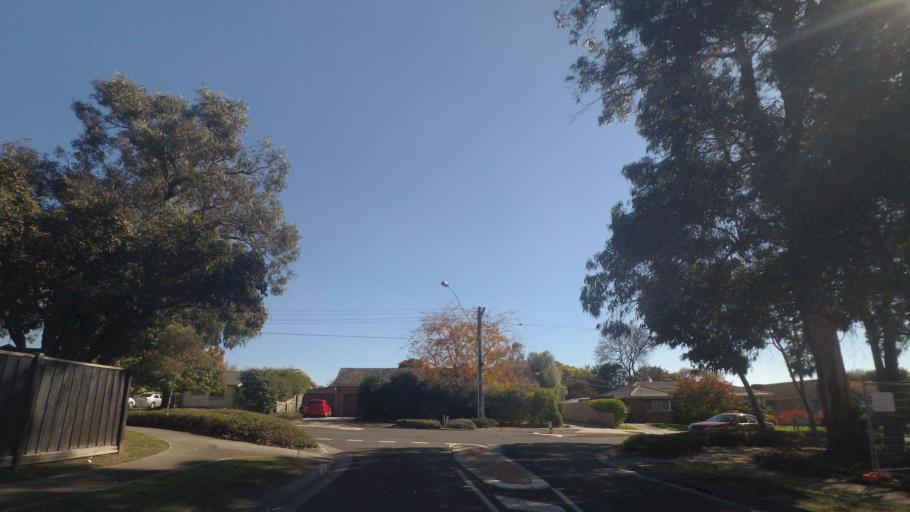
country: AU
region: Victoria
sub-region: Knox
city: Boronia
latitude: -37.8729
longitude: 145.2797
